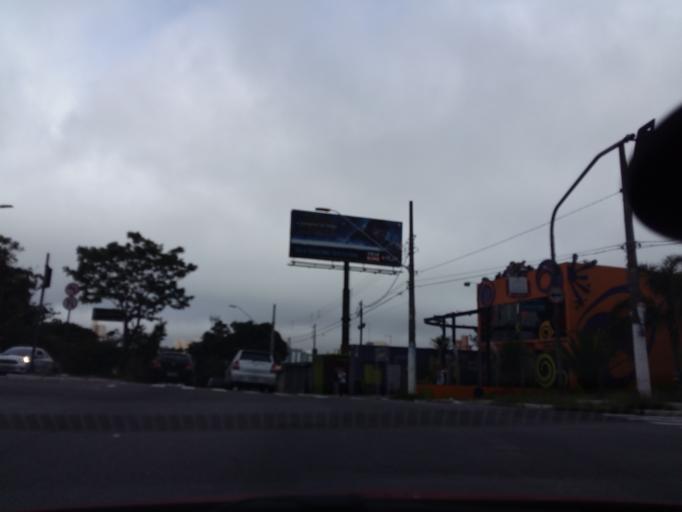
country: BR
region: Sao Paulo
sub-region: Santo Andre
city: Santo Andre
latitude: -23.6620
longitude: -46.5465
